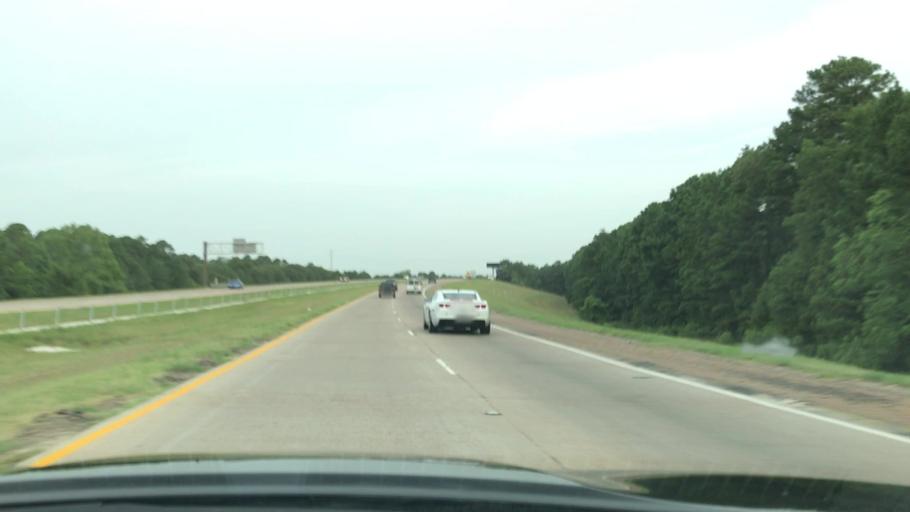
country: US
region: Louisiana
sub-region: Caddo Parish
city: Shreveport
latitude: 32.4179
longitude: -93.8253
